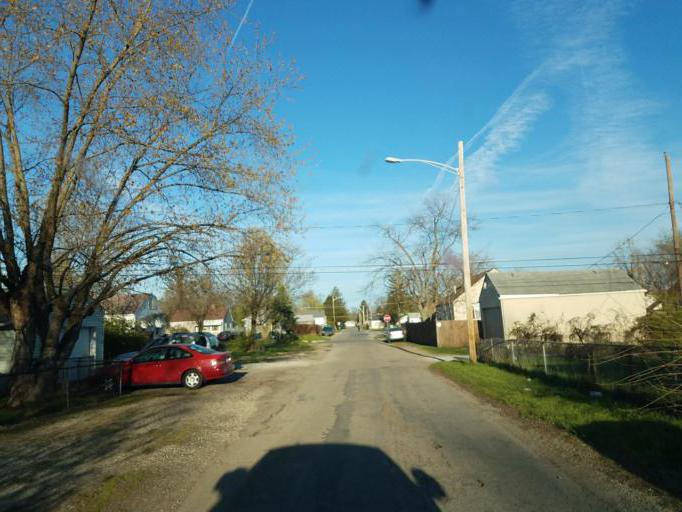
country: US
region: Ohio
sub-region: Franklin County
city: Columbus
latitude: 40.0176
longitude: -82.9907
